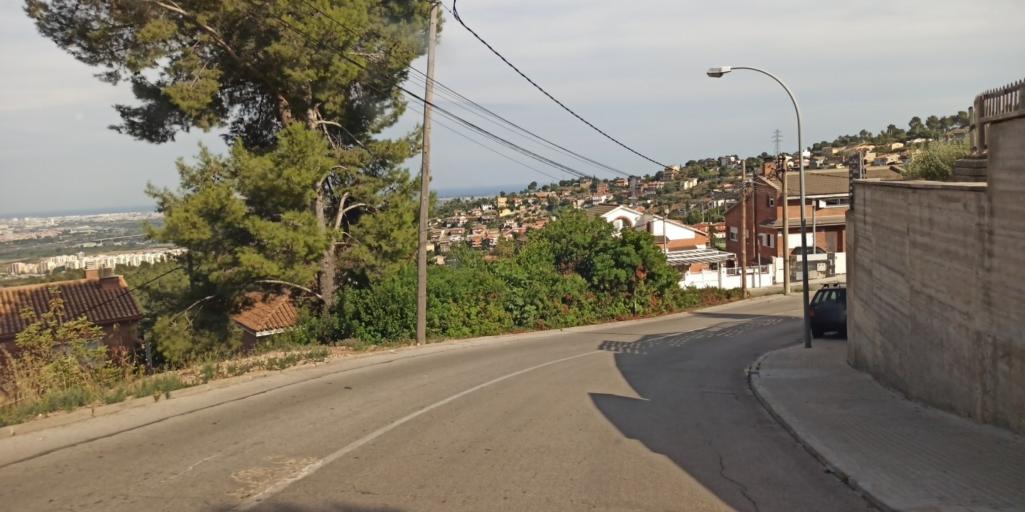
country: ES
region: Catalonia
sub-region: Provincia de Barcelona
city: Santa Coloma de Cervello
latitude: 41.3633
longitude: 2.0005
